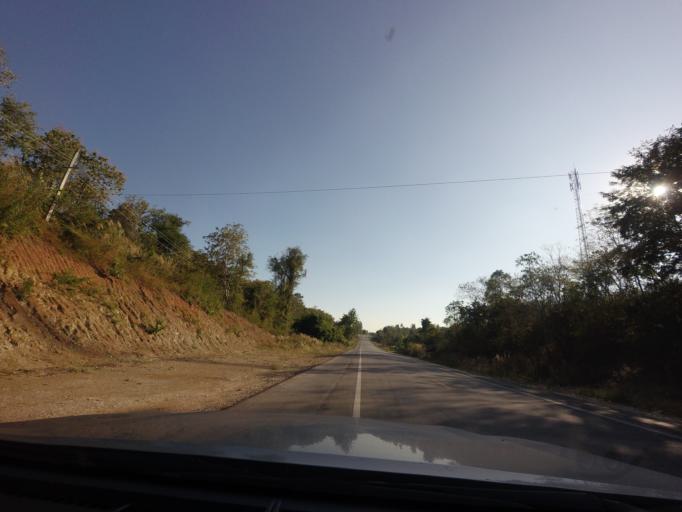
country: TH
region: Lampang
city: Mae Mo
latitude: 18.4817
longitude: 99.6356
